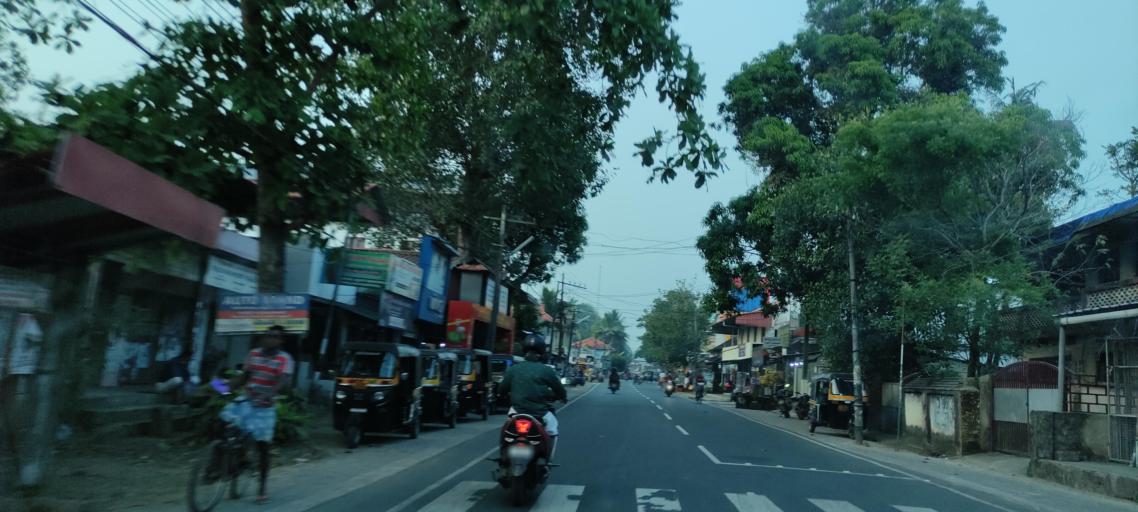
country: IN
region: Kerala
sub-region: Alappuzha
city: Mavelikara
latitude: 9.3081
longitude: 76.5341
